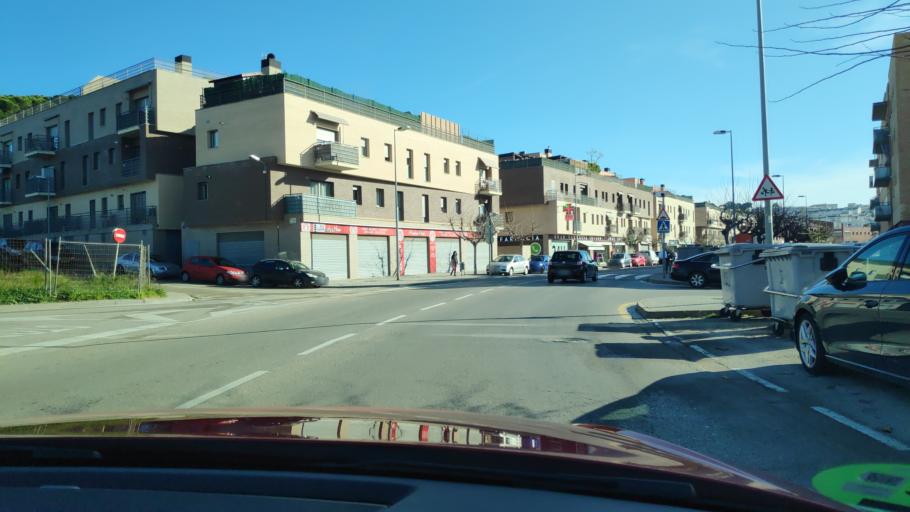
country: ES
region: Catalonia
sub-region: Provincia de Girona
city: Lloret de Mar
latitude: 41.7101
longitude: 2.8384
